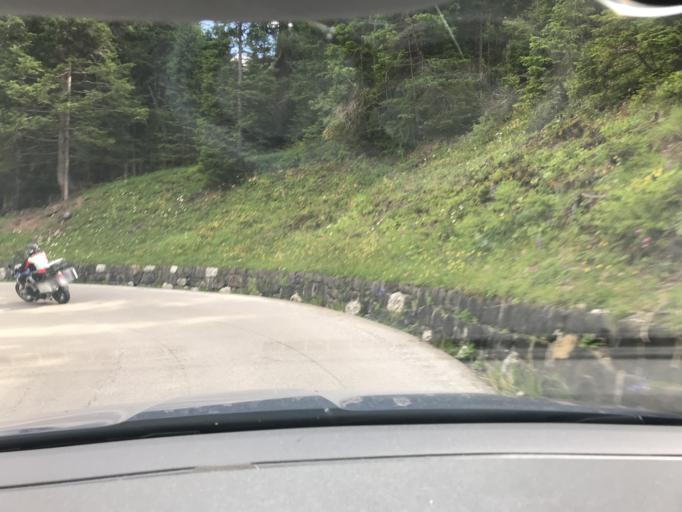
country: IT
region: Veneto
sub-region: Provincia di Belluno
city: Livinallongo del Col di Lana
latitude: 46.5031
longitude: 11.9924
